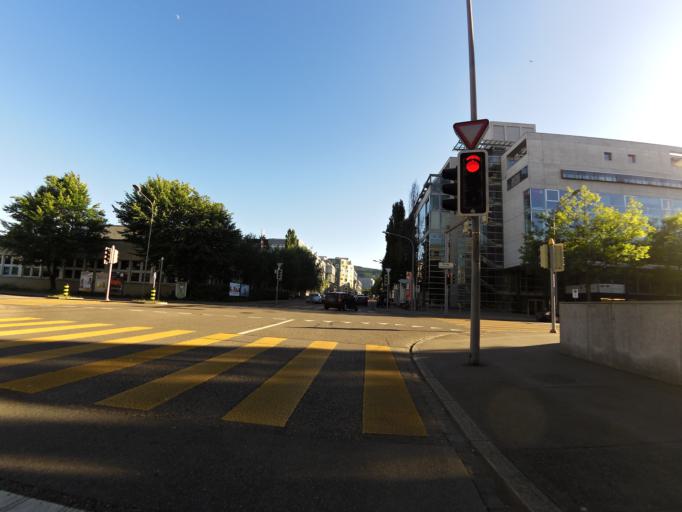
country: CH
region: Zurich
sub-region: Bezirk Zuerich
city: Zuerich (Kreis 9) / Altstetten
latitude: 47.3867
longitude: 8.4966
